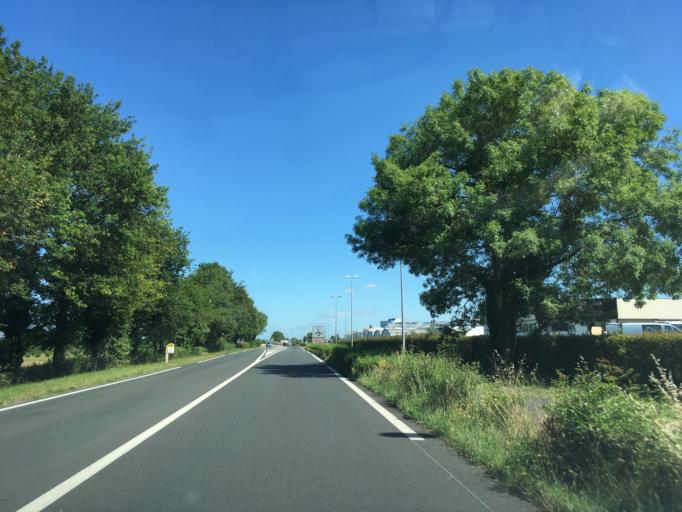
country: FR
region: Pays de la Loire
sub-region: Departement de la Vendee
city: Saint-Georges-de-Montaigu
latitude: 46.9552
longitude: -1.3050
